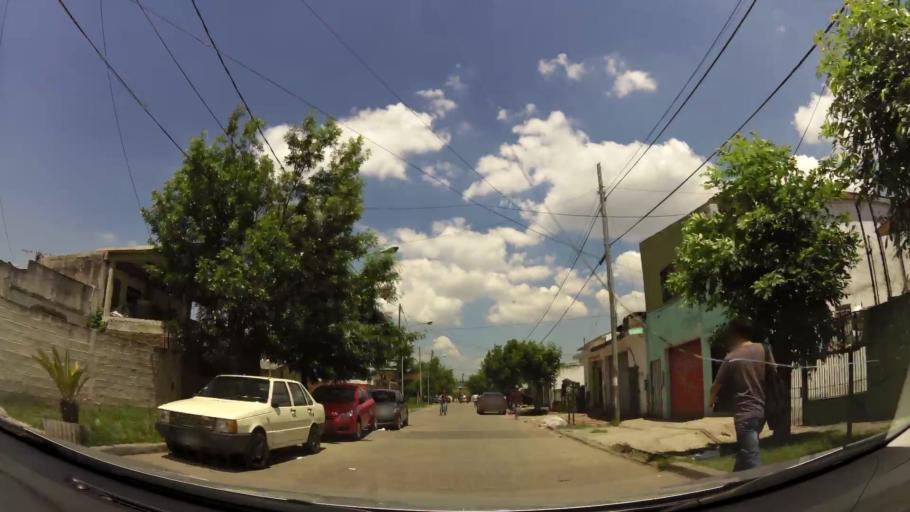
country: AR
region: Buenos Aires
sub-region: Partido de Tigre
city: Tigre
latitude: -34.4125
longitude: -58.6044
